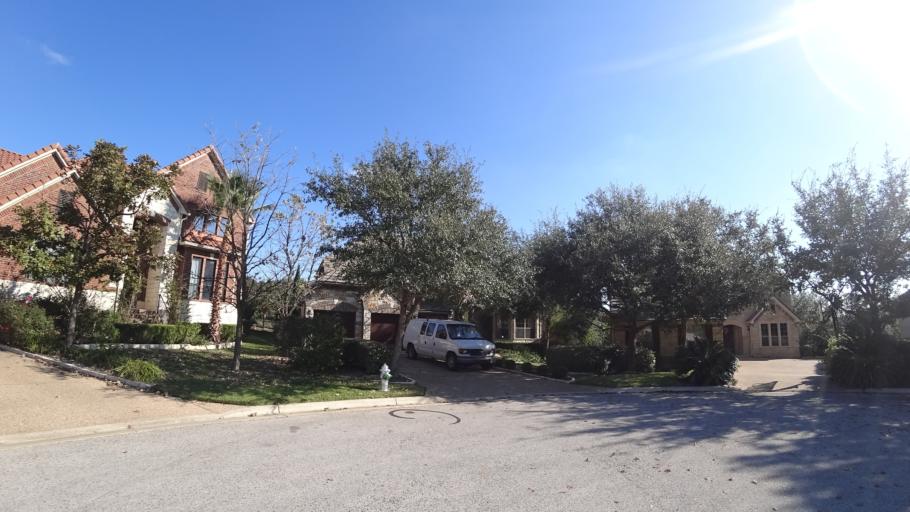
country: US
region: Texas
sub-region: Travis County
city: Barton Creek
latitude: 30.3536
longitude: -97.8876
